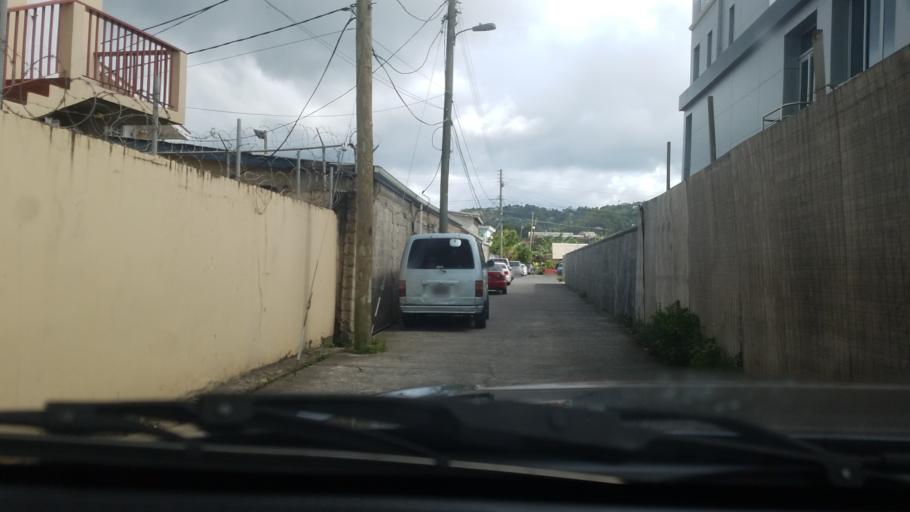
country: LC
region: Castries Quarter
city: Bisee
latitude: 14.0201
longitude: -60.9902
